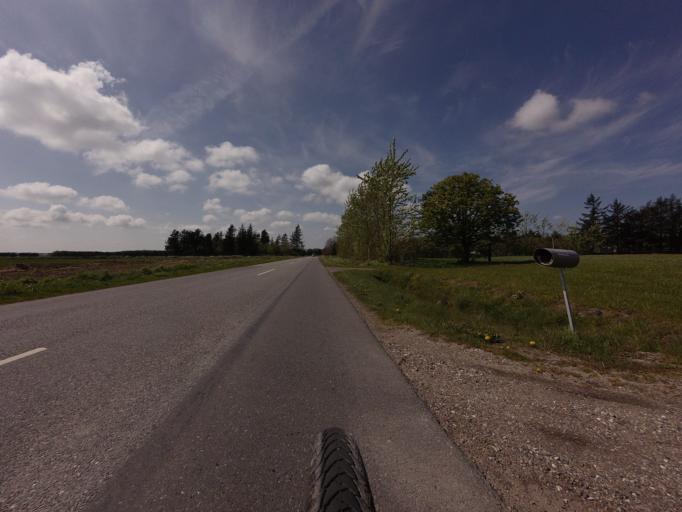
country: DK
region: North Denmark
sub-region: Jammerbugt Kommune
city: Brovst
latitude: 57.1436
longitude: 9.5325
